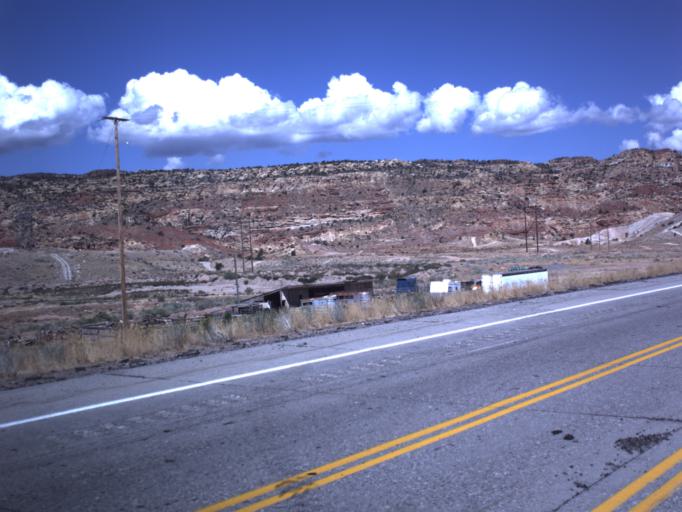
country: US
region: Utah
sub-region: Sevier County
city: Richfield
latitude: 38.7601
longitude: -112.1054
